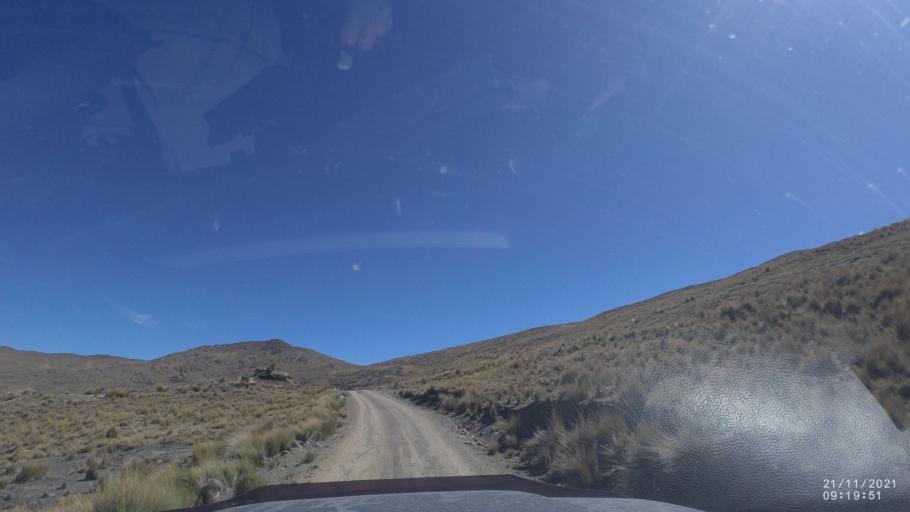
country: BO
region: Cochabamba
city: Cochabamba
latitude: -17.1127
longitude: -66.2521
